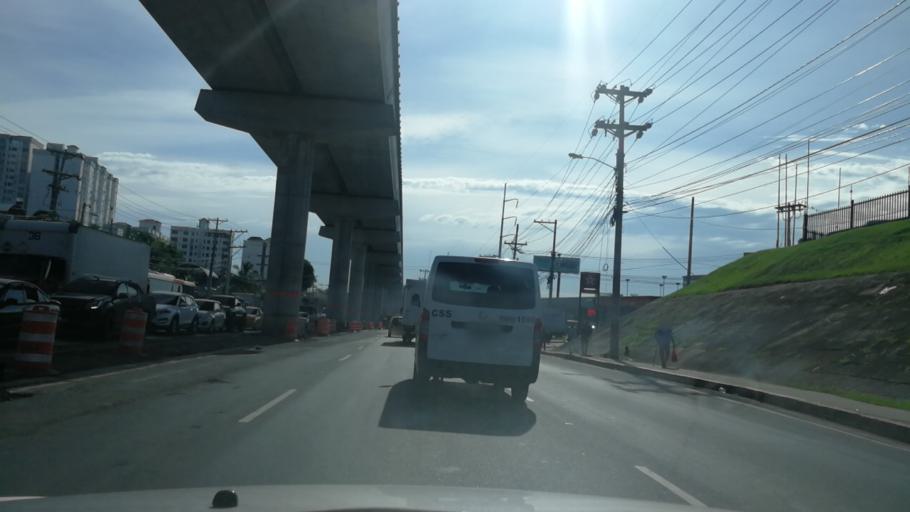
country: PA
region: Panama
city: San Miguelito
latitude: 9.0450
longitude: -79.4691
